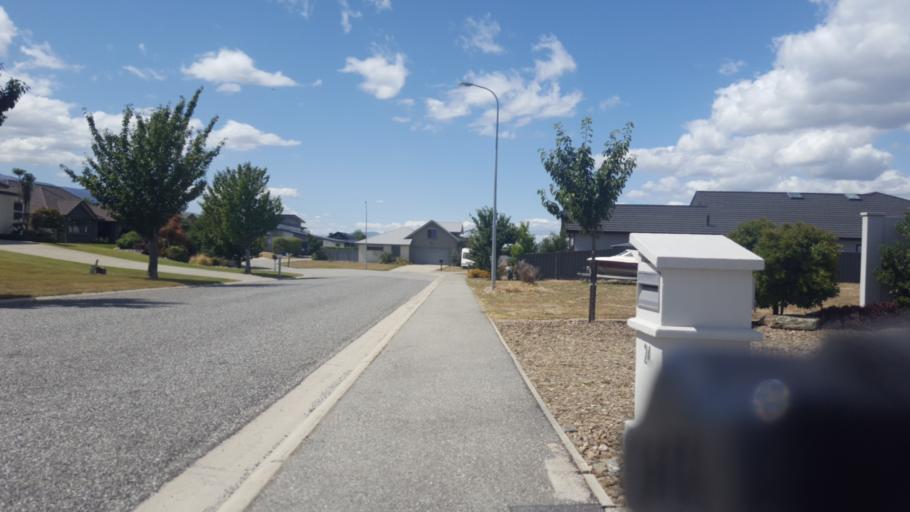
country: NZ
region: Otago
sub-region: Queenstown-Lakes District
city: Wanaka
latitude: -44.9718
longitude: 169.2487
